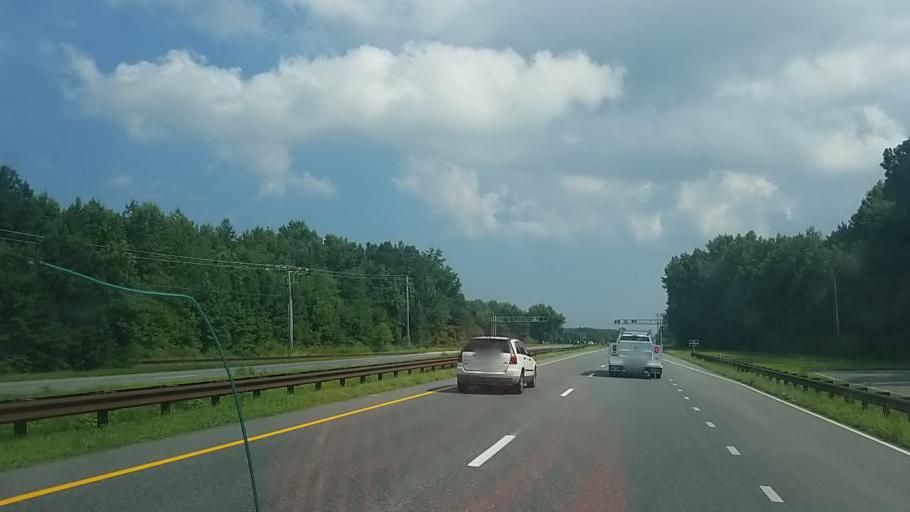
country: US
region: Delaware
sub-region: Sussex County
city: Selbyville
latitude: 38.4366
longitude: -75.2242
